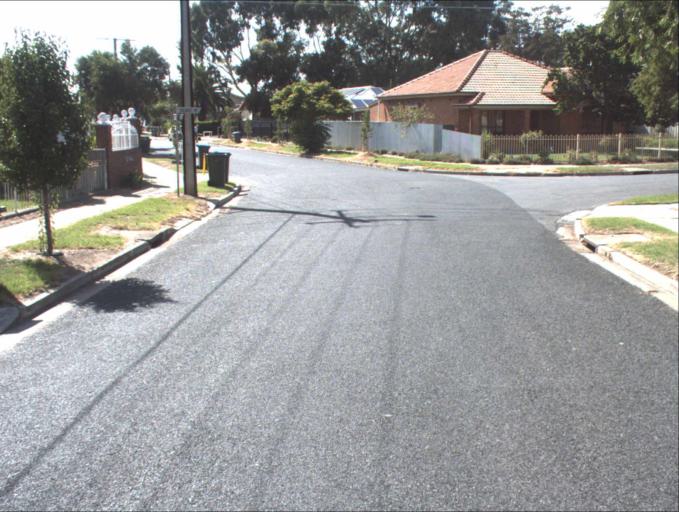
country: AU
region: South Australia
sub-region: Prospect
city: Prospect
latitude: -34.8801
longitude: 138.5747
